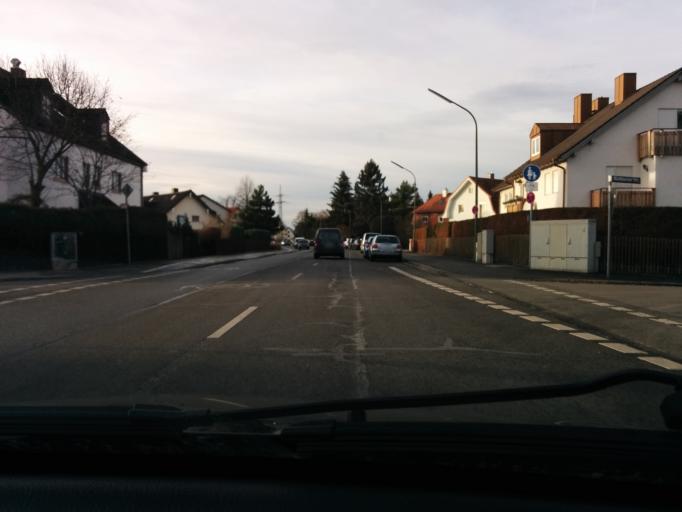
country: DE
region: Bavaria
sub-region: Upper Bavaria
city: Pasing
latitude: 48.1516
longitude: 11.4317
